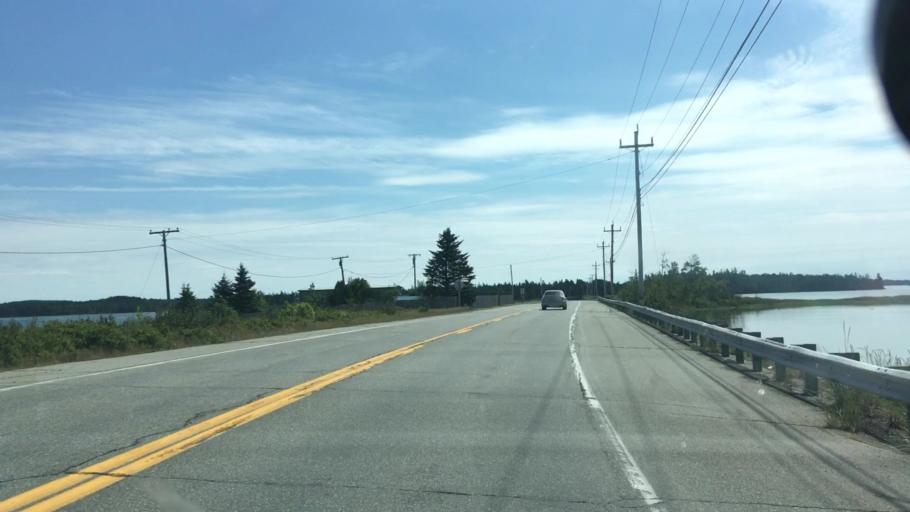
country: US
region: Maine
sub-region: Washington County
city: Eastport
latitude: 44.9532
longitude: -67.0394
